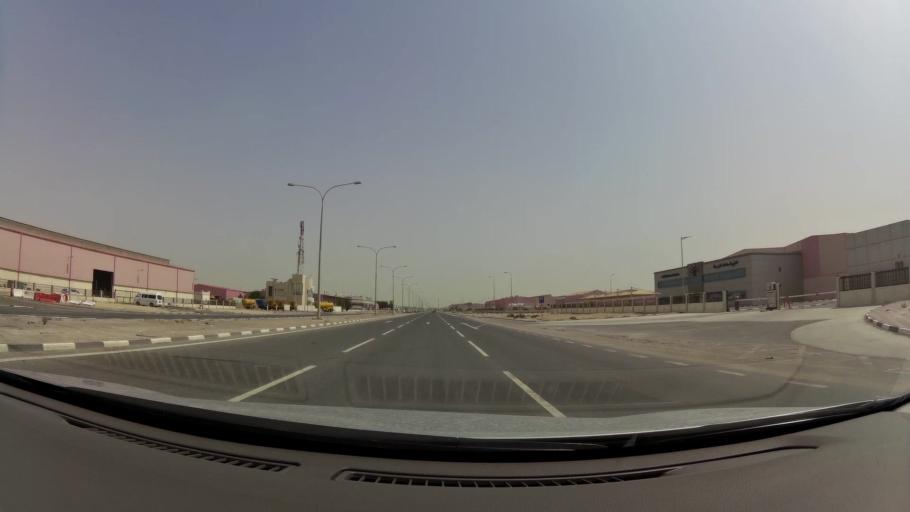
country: QA
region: Al Wakrah
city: Al Wukayr
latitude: 25.1549
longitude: 51.4010
